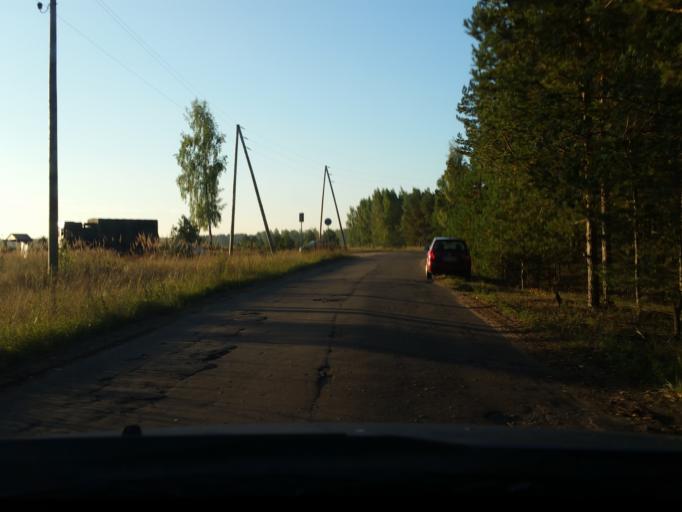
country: LV
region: Adazi
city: Adazi
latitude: 57.1182
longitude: 24.3628
